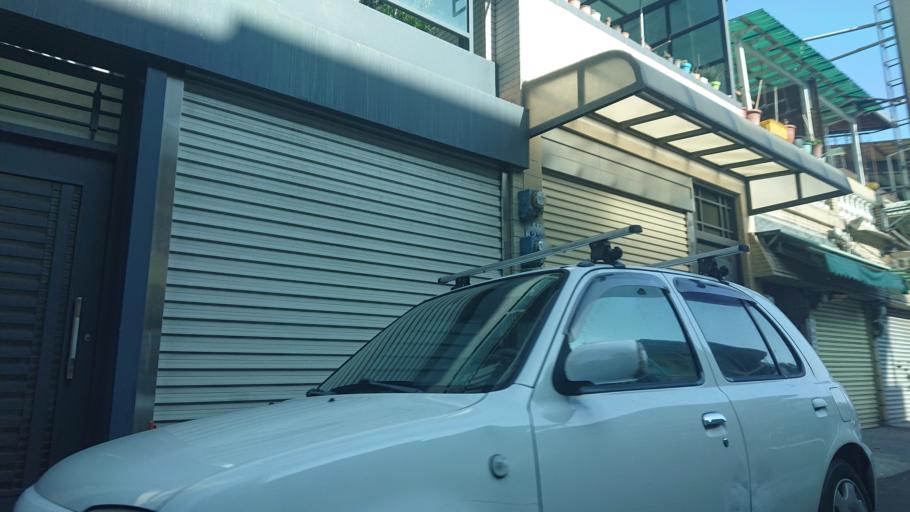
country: TW
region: Taiwan
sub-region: Tainan
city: Tainan
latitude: 23.0126
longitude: 120.2323
